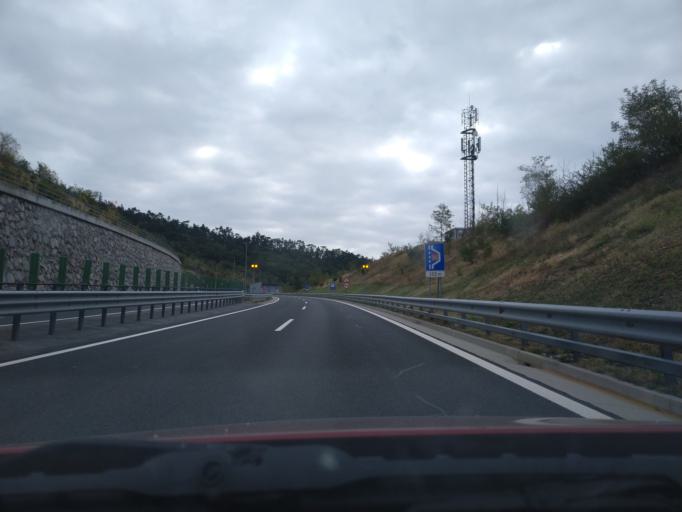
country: SI
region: Vipava
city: Vipava
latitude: 45.8048
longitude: 13.9781
